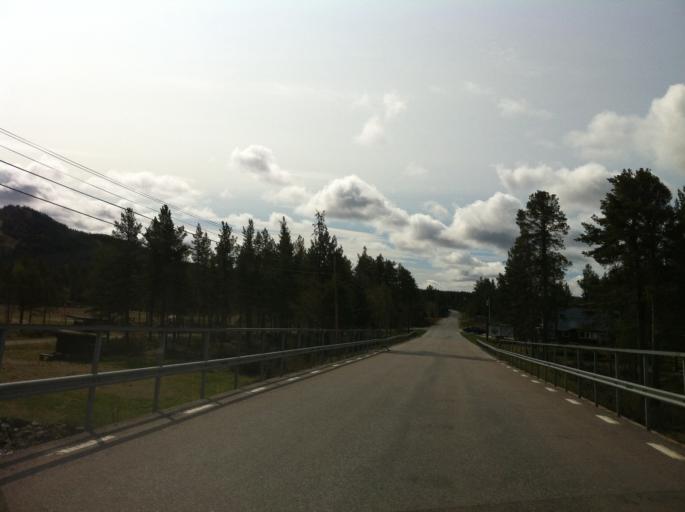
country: NO
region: Hedmark
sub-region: Engerdal
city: Engerdal
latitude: 62.4420
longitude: 12.6830
